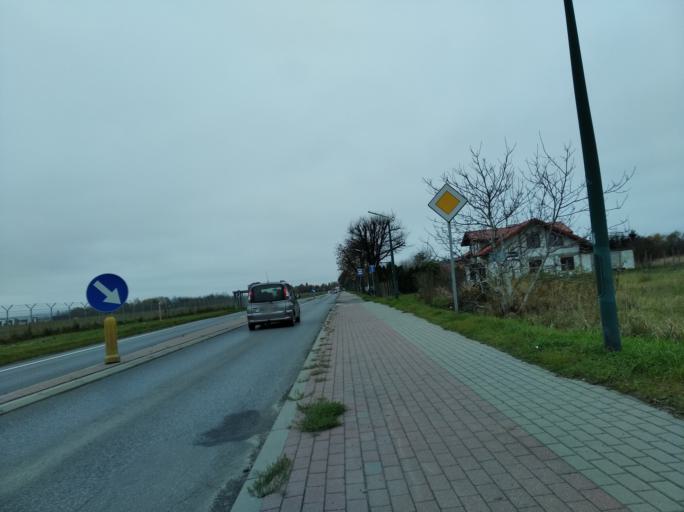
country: PL
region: Subcarpathian Voivodeship
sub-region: Krosno
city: Krosno
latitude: 49.6873
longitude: 21.7246
